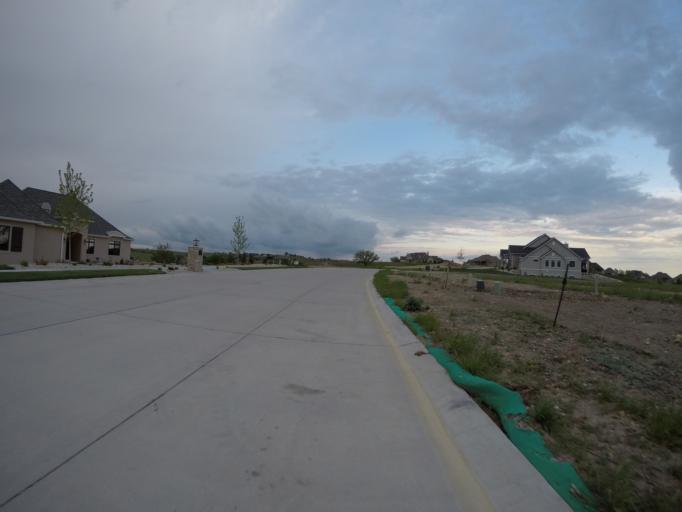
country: US
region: Kansas
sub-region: Riley County
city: Manhattan
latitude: 39.2165
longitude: -96.6297
